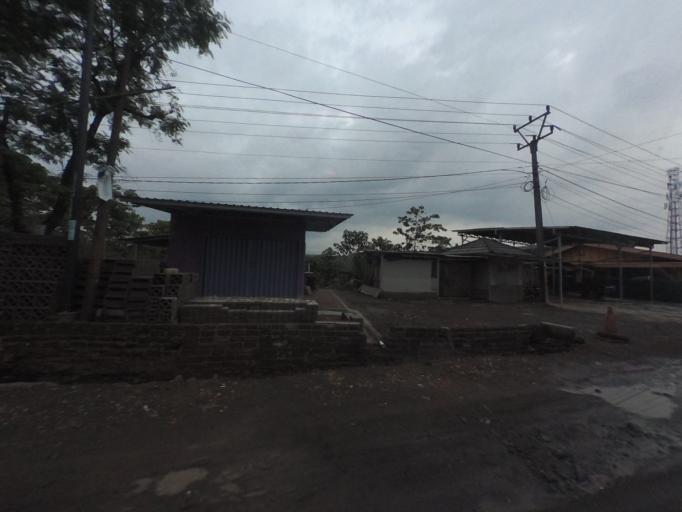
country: ID
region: West Java
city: Cicurug
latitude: -6.8348
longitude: 106.7604
